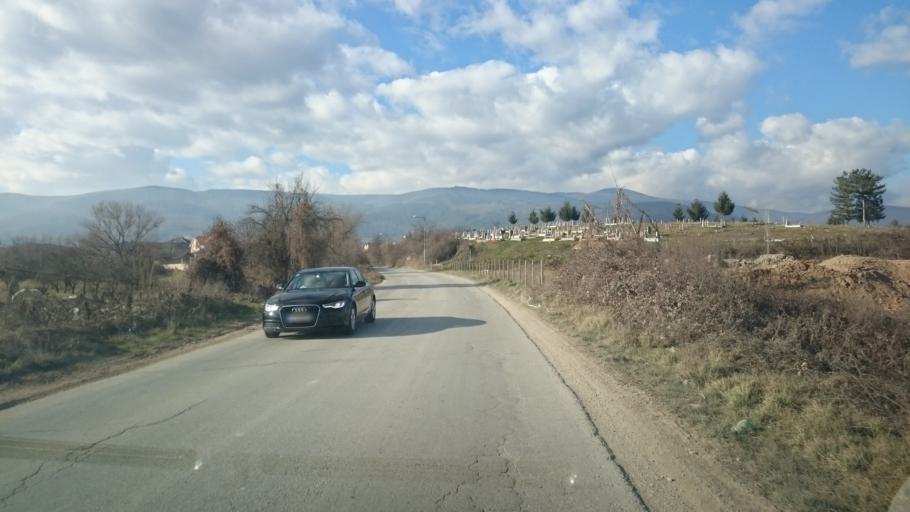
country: MK
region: Kicevo
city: Kicevo
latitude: 41.4992
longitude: 20.9604
